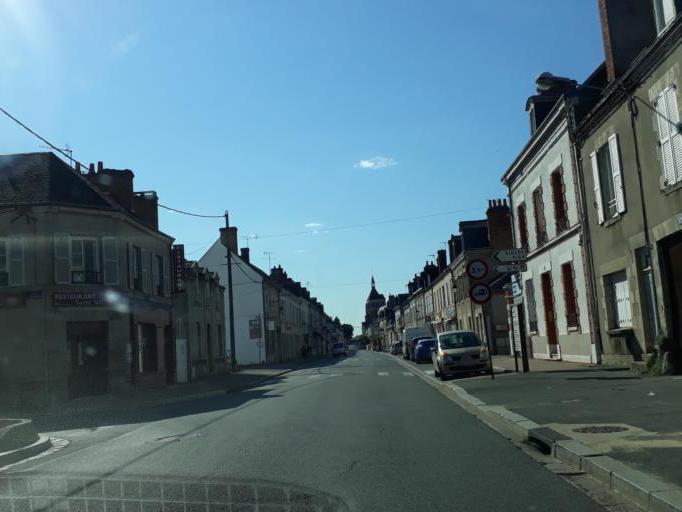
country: FR
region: Centre
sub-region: Departement du Loiret
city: Chateauneuf-sur-Loire
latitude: 47.8628
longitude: 2.2249
